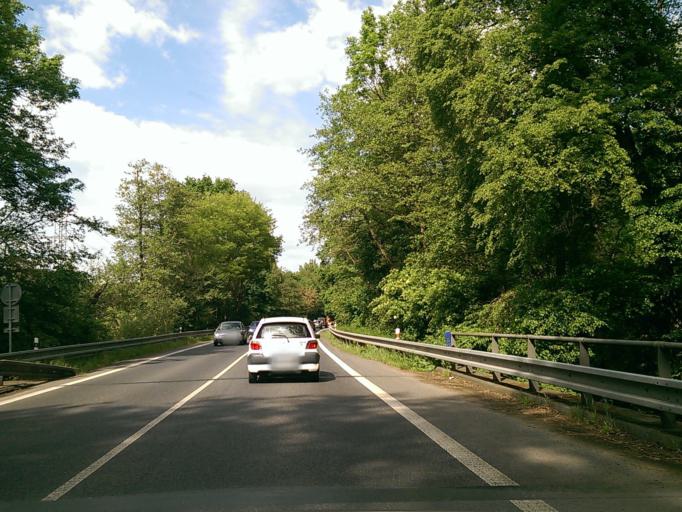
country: CZ
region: Central Bohemia
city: Libis
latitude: 50.2934
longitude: 14.4989
